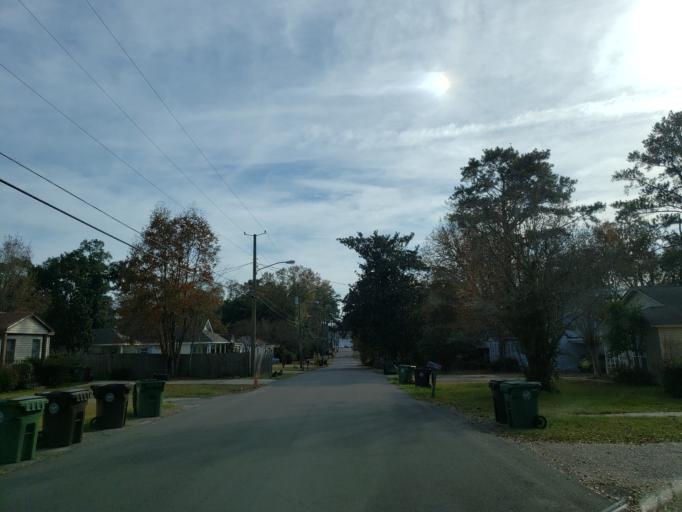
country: US
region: Mississippi
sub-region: Forrest County
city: Hattiesburg
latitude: 31.3280
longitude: -89.3193
